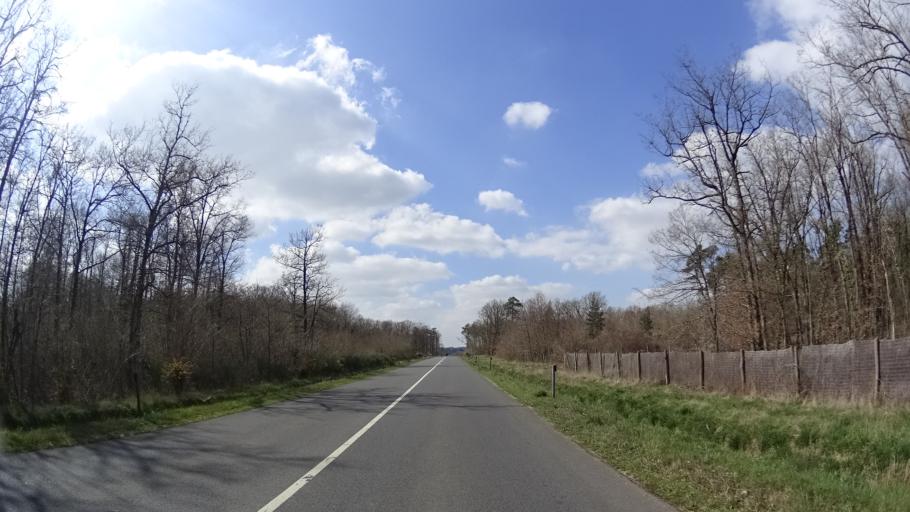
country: FR
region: Pays de la Loire
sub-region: Departement de Maine-et-Loire
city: Breze
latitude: 47.0891
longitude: -0.0045
